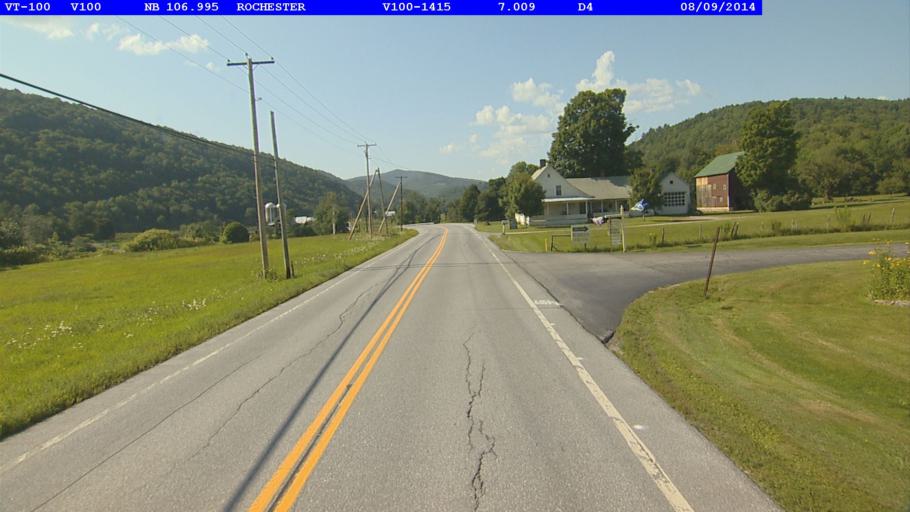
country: US
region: Vermont
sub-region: Orange County
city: Randolph
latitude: 43.8958
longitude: -72.8195
